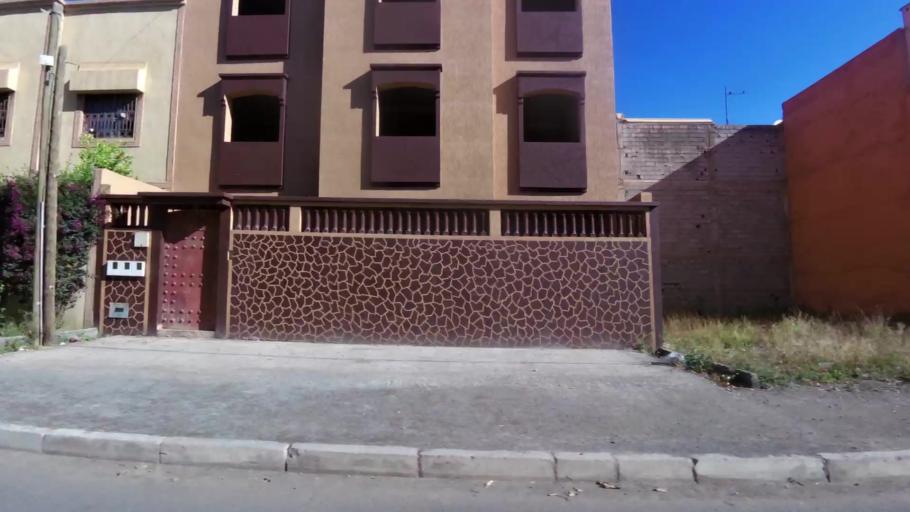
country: MA
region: Marrakech-Tensift-Al Haouz
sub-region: Marrakech
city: Marrakesh
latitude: 31.5904
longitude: -8.0244
